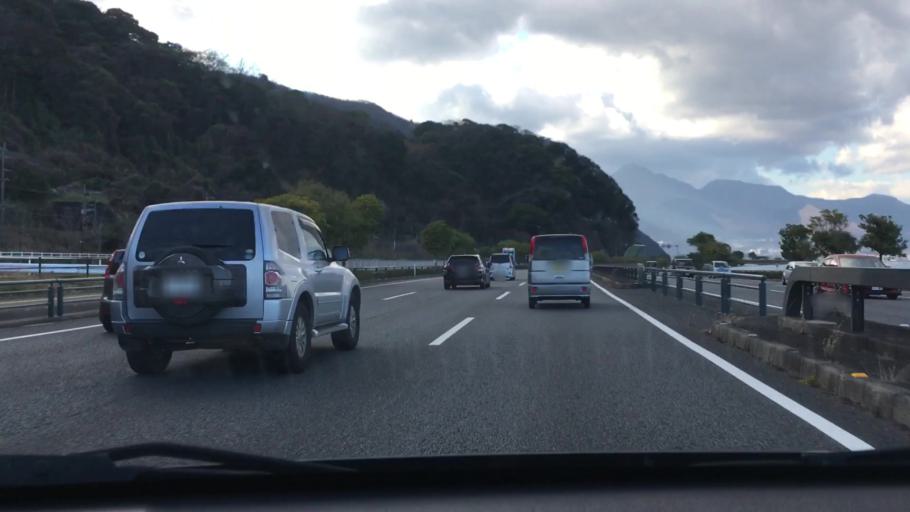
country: JP
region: Oita
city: Oita
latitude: 33.2555
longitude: 131.5586
